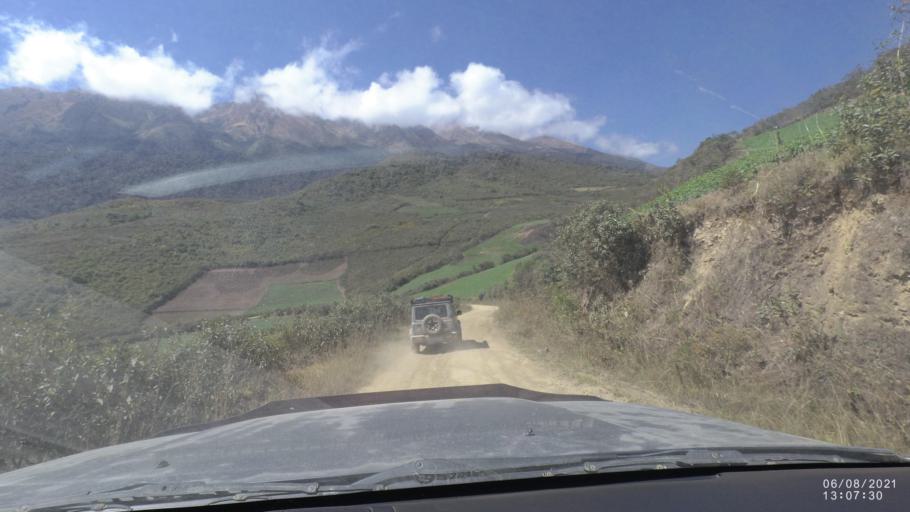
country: BO
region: La Paz
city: Quime
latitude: -16.7310
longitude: -66.7076
